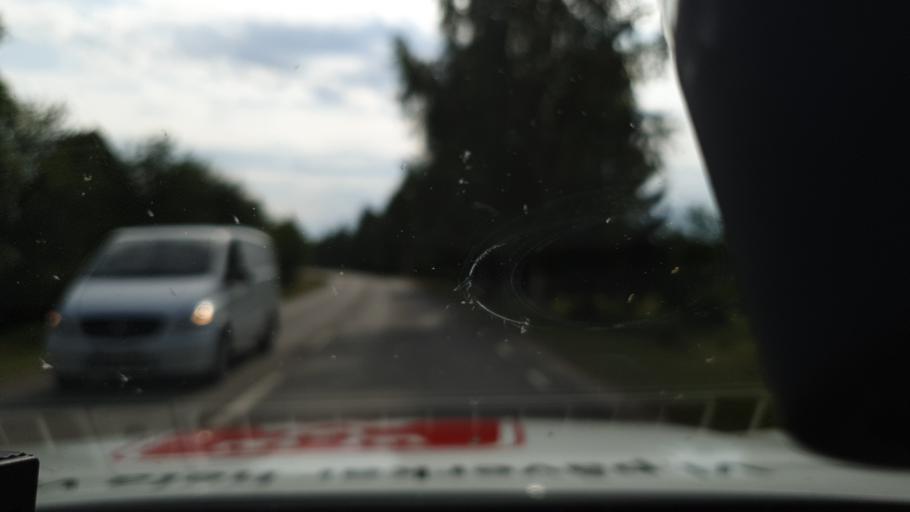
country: SE
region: Norrbotten
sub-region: Lulea Kommun
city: Ranea
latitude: 65.8543
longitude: 22.2802
